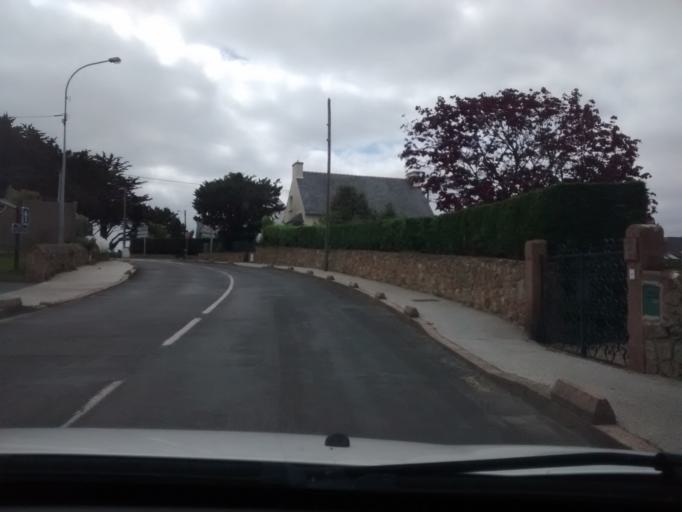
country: FR
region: Brittany
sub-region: Departement des Cotes-d'Armor
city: Tregastel
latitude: 48.8172
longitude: -3.4734
